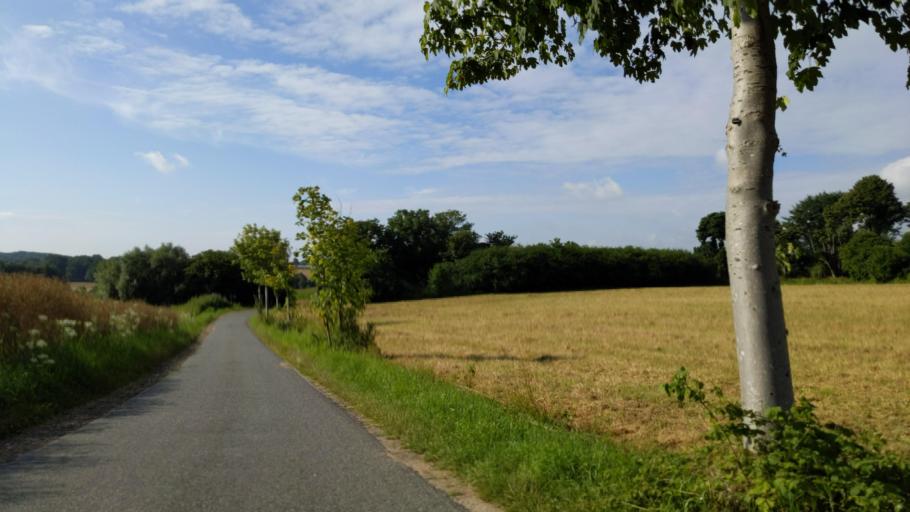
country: DE
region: Schleswig-Holstein
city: Bad Schwartau
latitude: 53.9698
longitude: 10.6662
